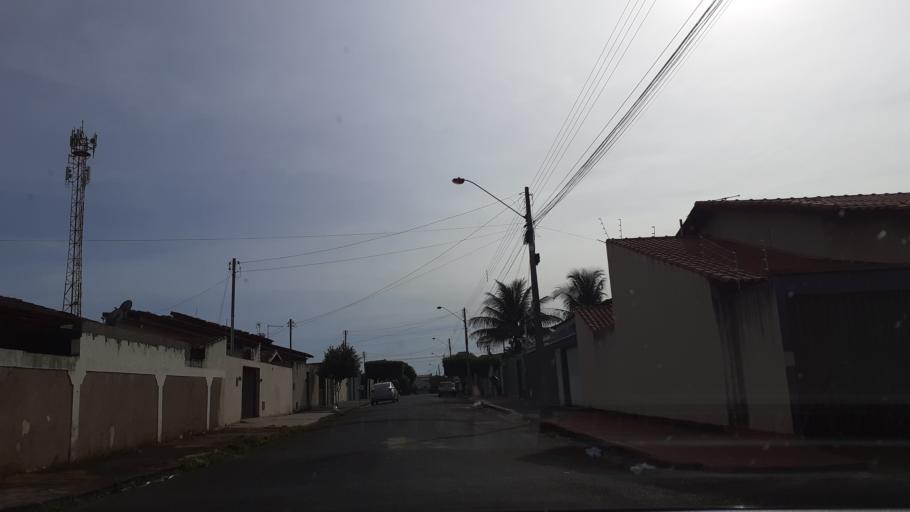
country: BR
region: Goias
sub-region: Itumbiara
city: Itumbiara
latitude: -18.4179
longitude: -49.2458
